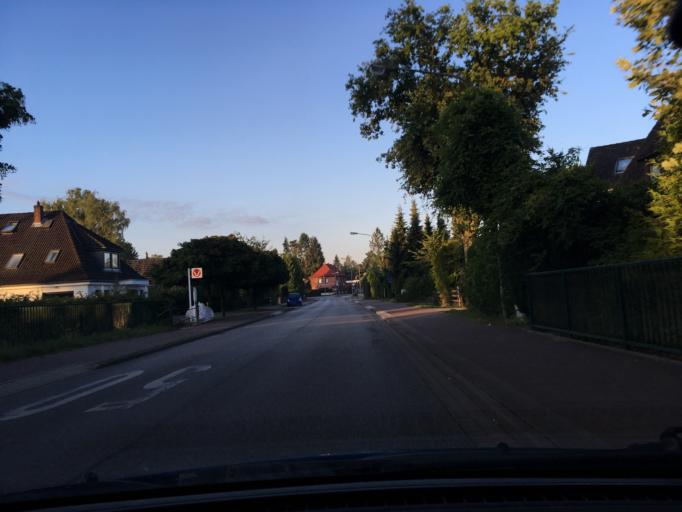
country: DE
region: Lower Saxony
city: Harmstorf
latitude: 53.3791
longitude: 10.0356
